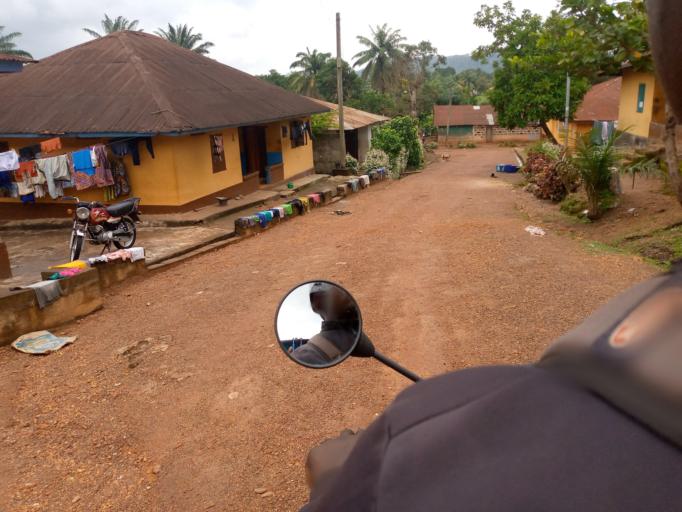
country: SL
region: Eastern Province
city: Kenema
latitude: 7.8629
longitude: -11.1883
